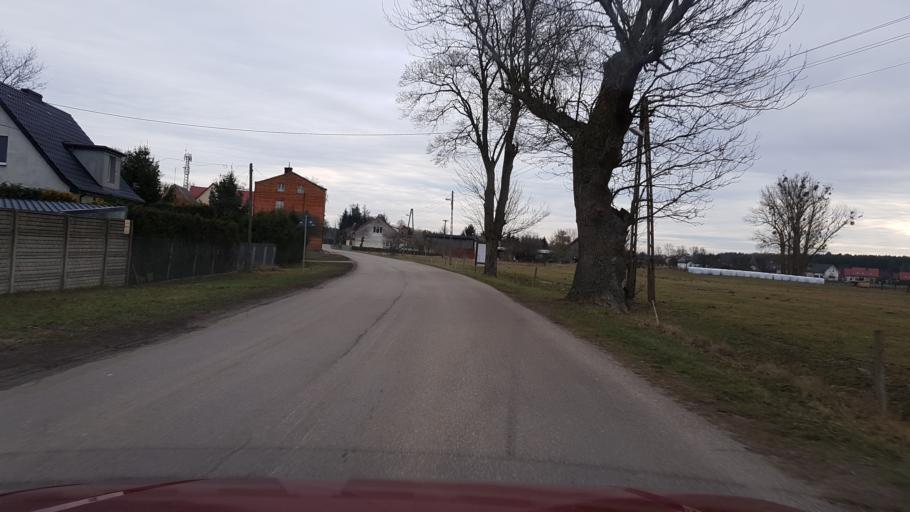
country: PL
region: West Pomeranian Voivodeship
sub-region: Powiat policki
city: Dobra
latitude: 53.5485
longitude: 14.4602
